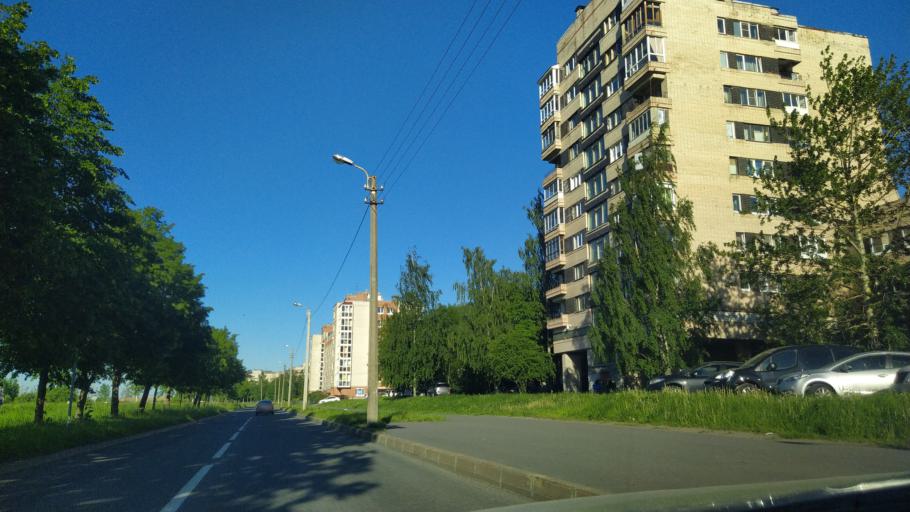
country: RU
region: St.-Petersburg
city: Pushkin
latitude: 59.7411
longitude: 30.4062
